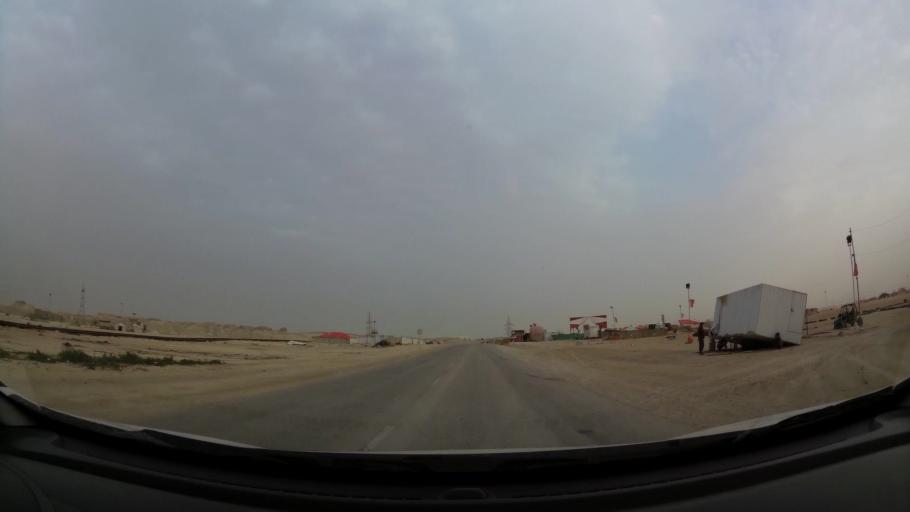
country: BH
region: Central Governorate
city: Dar Kulayb
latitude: 26.0050
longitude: 50.5843
